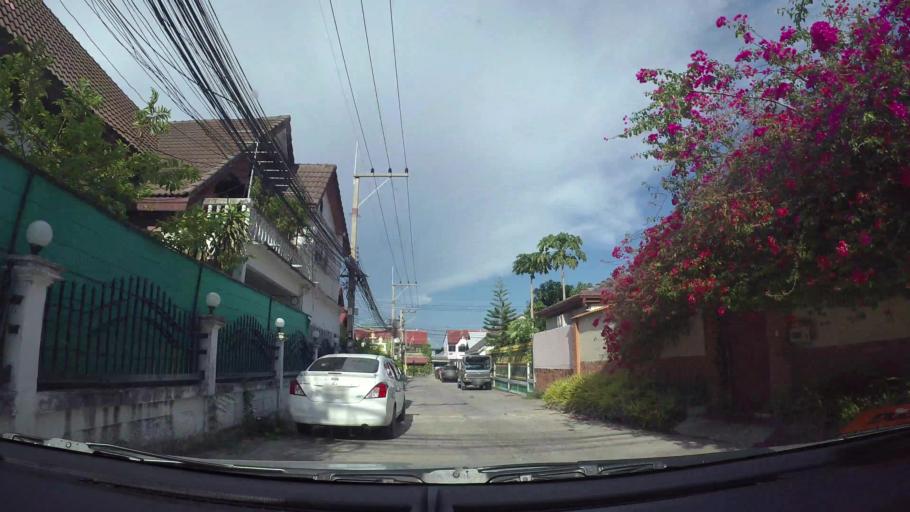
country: TH
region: Chon Buri
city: Phatthaya
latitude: 12.9158
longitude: 100.8739
